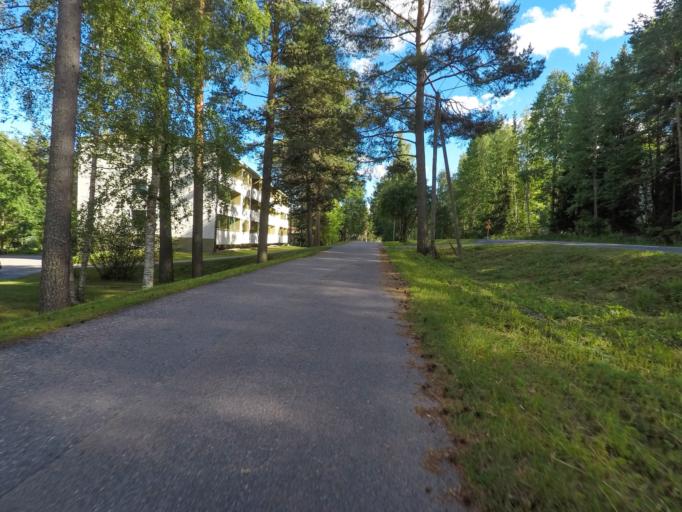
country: FI
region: South Karelia
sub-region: Lappeenranta
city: Lappeenranta
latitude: 61.0830
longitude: 28.1481
